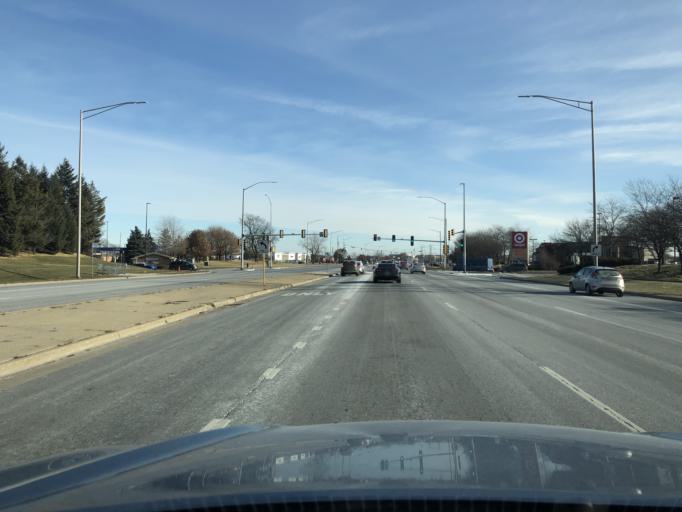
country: US
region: Illinois
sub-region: Lake County
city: Grandwood Park
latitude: 42.3855
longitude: -87.9673
